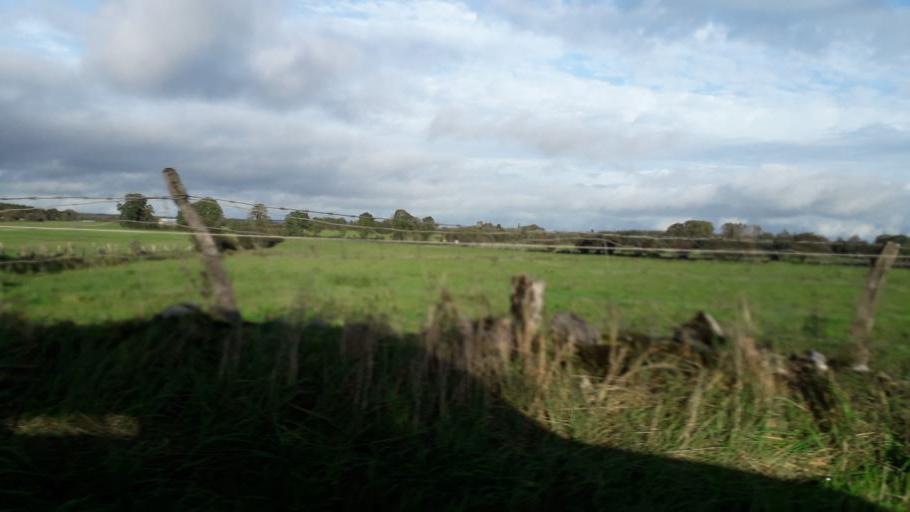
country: IE
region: Connaught
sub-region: Roscommon
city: Castlerea
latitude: 53.8656
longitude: -8.4019
